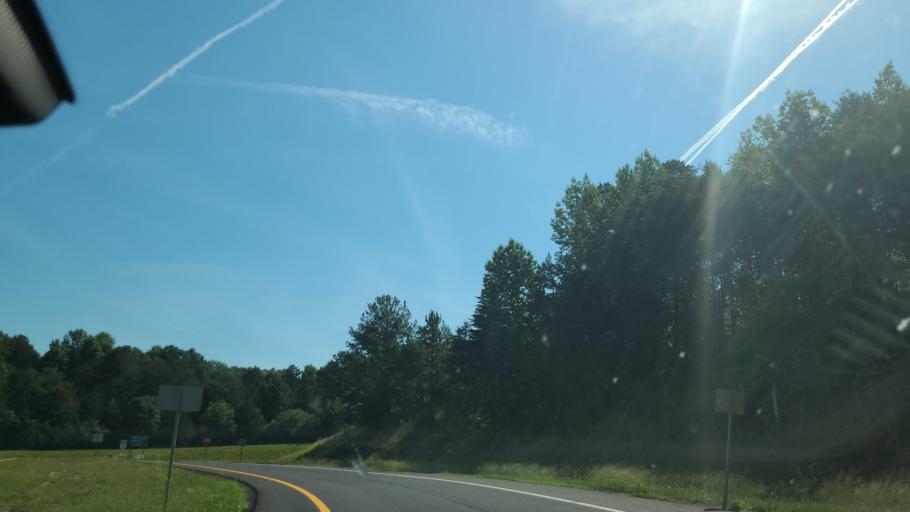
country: US
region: Georgia
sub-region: Franklin County
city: Gumlog
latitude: 34.4887
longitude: -83.0210
